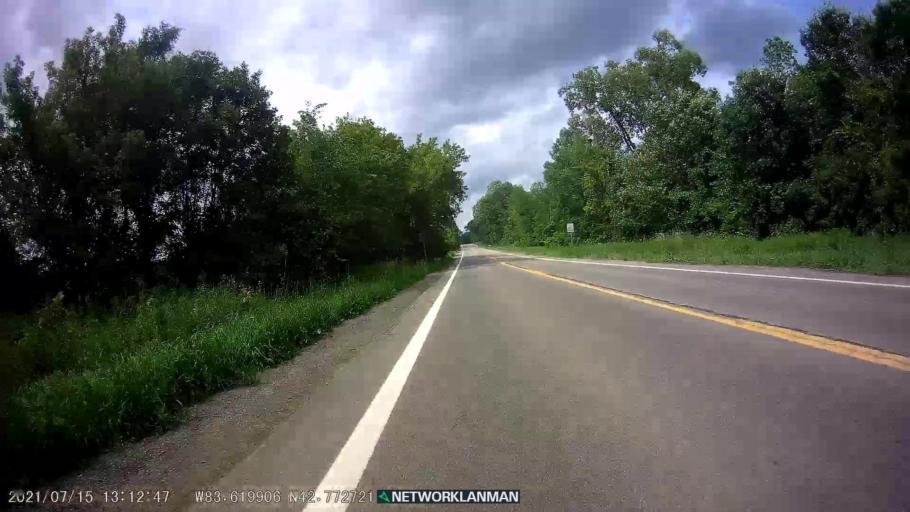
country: US
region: Michigan
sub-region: Oakland County
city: Holly
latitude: 42.7725
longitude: -83.6199
